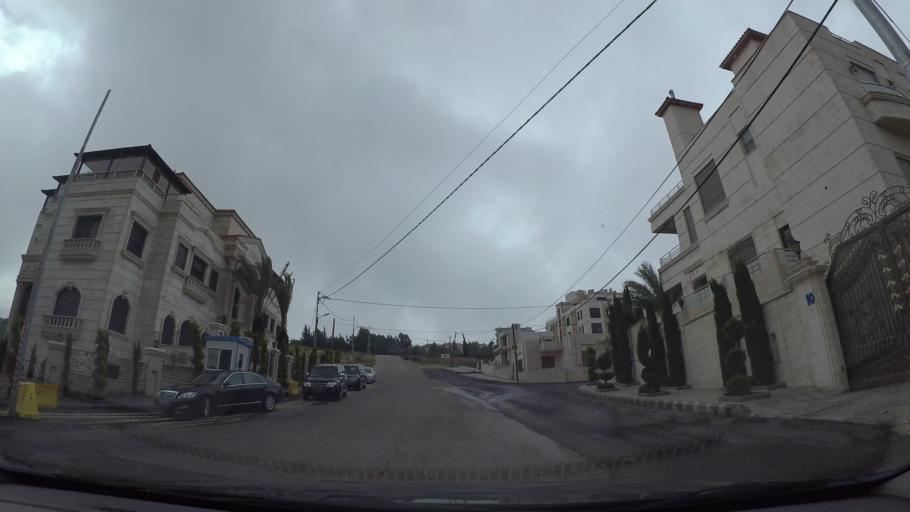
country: JO
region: Amman
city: Umm as Summaq
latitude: 31.9172
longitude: 35.8649
